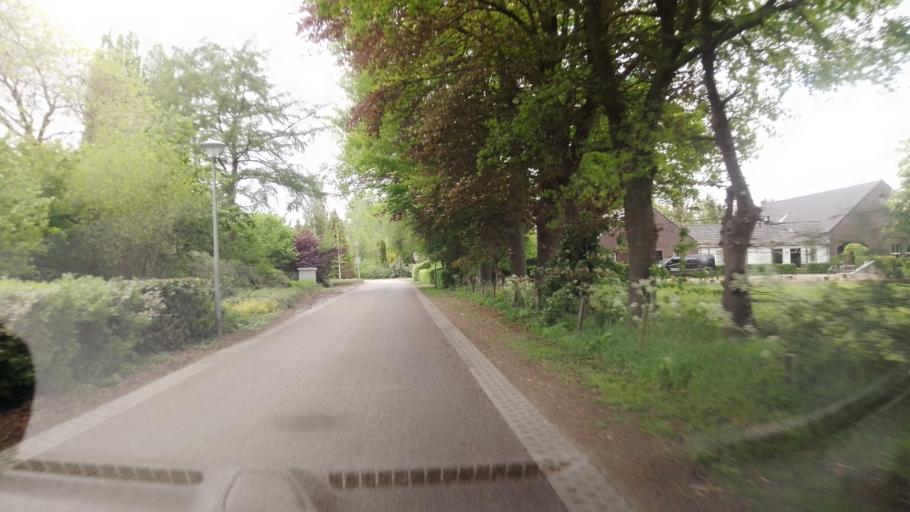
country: NL
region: Limburg
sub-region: Gemeente Bergen
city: Wellerlooi
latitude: 51.4936
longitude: 6.1238
